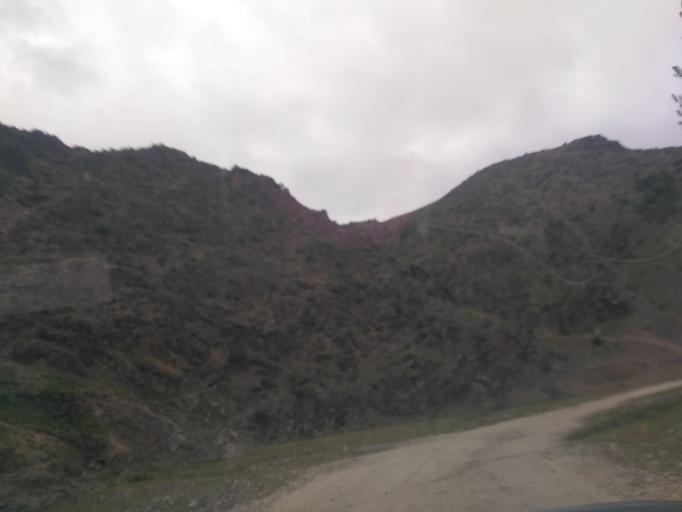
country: UZ
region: Jizzax
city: Zomin
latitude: 39.8524
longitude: 68.3949
